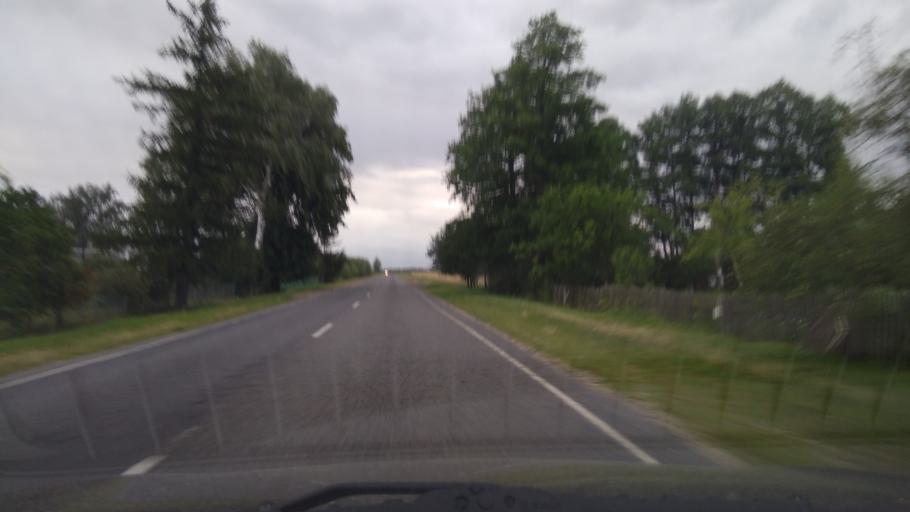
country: BY
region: Brest
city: Byaroza
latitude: 52.4264
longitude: 24.9810
